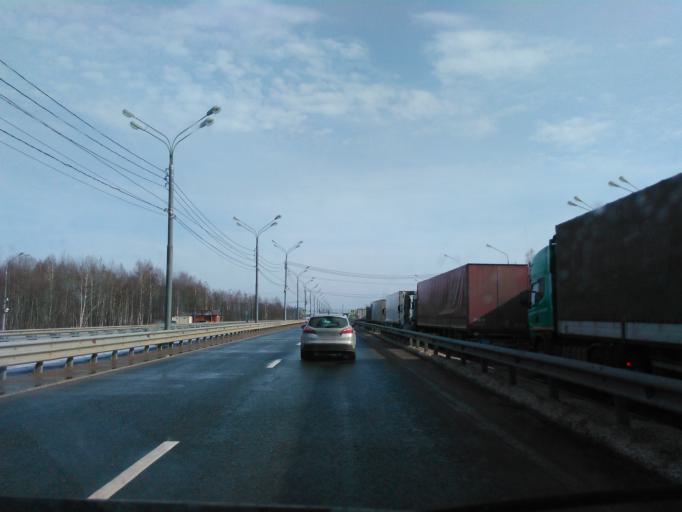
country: RU
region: Smolensk
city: Rudnya
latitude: 54.6909
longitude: 31.0014
